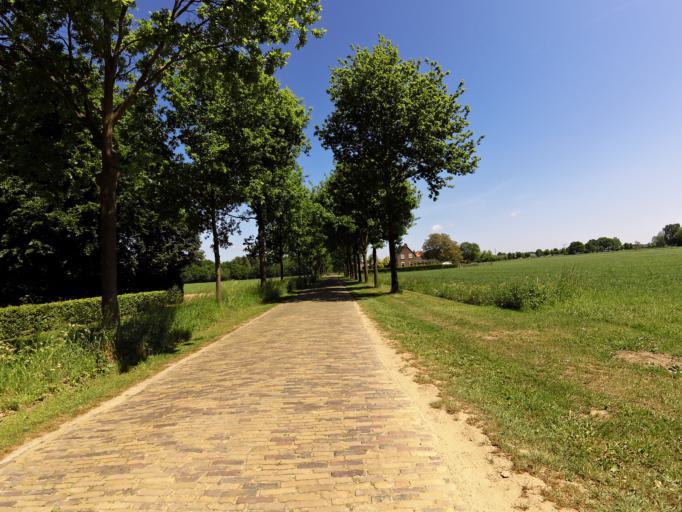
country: NL
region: Gelderland
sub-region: Gemeente Bronckhorst
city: Baak
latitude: 52.0636
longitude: 6.2358
